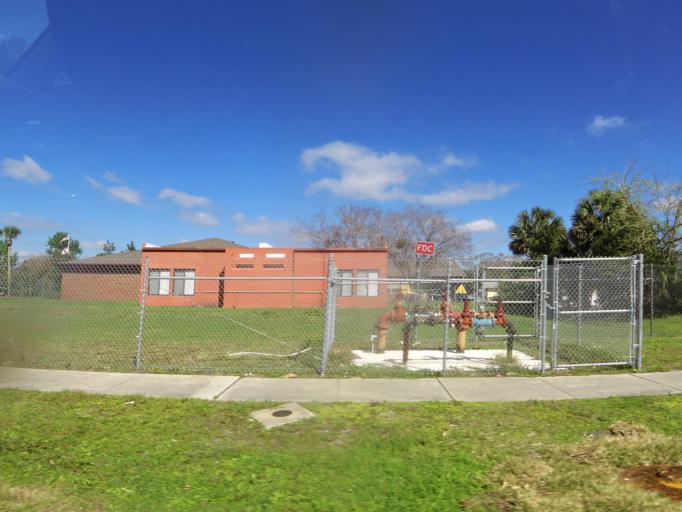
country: US
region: Florida
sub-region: Seminole County
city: Sanford
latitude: 28.8013
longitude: -81.2567
